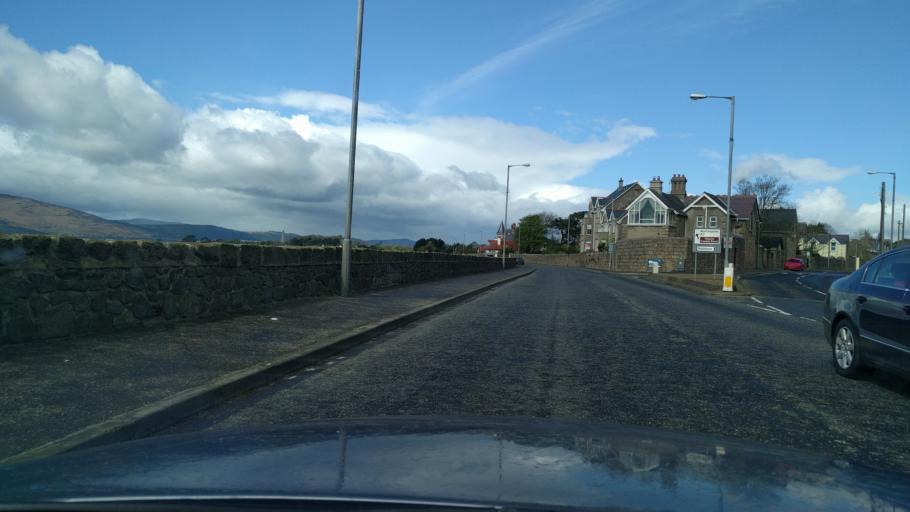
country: GB
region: Northern Ireland
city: Rostrevor
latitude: 54.0953
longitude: -6.1925
